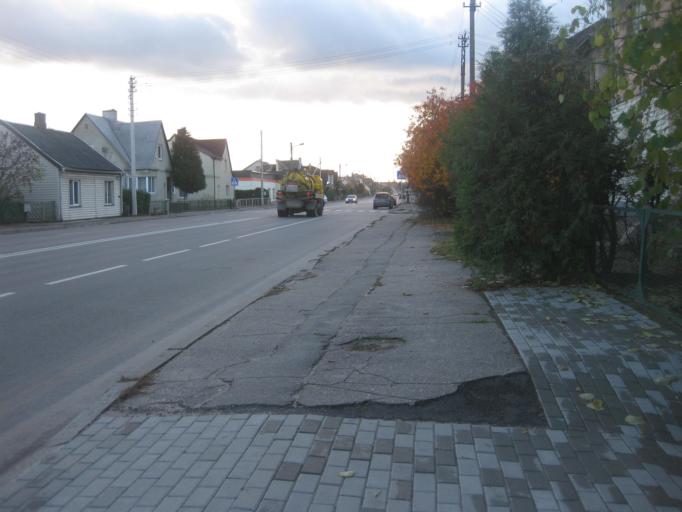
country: LT
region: Kauno apskritis
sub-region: Kaunas
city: Silainiai
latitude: 54.9240
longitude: 23.9020
